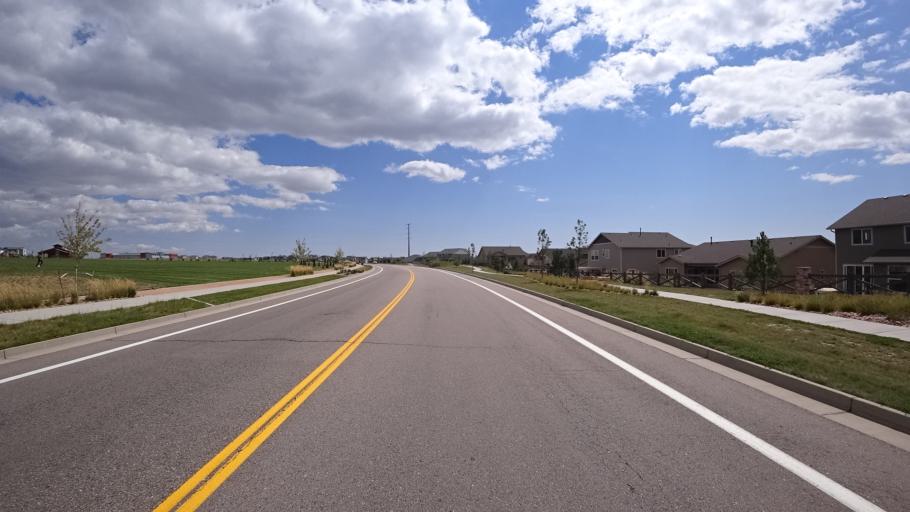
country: US
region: Colorado
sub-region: El Paso County
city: Cimarron Hills
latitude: 38.9313
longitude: -104.6665
